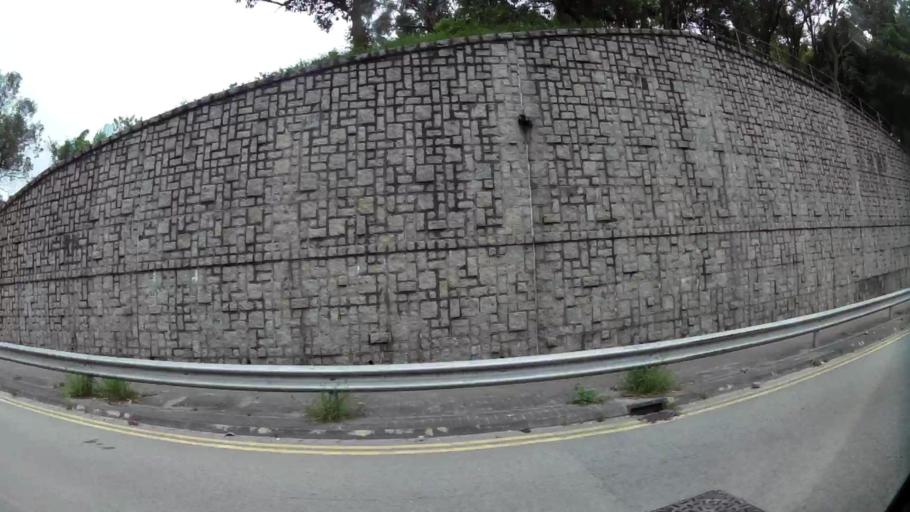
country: HK
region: Tuen Mun
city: Tuen Mun
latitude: 22.4135
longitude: 113.9804
